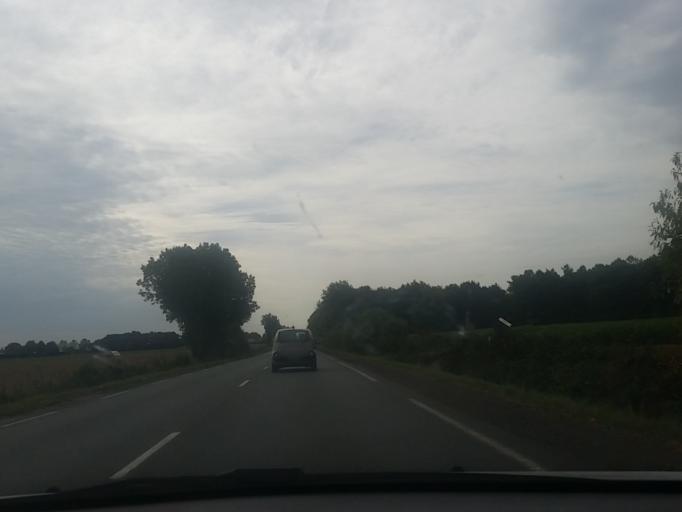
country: FR
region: Pays de la Loire
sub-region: Departement de la Vendee
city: Vendrennes
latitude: 46.8160
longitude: -1.1447
